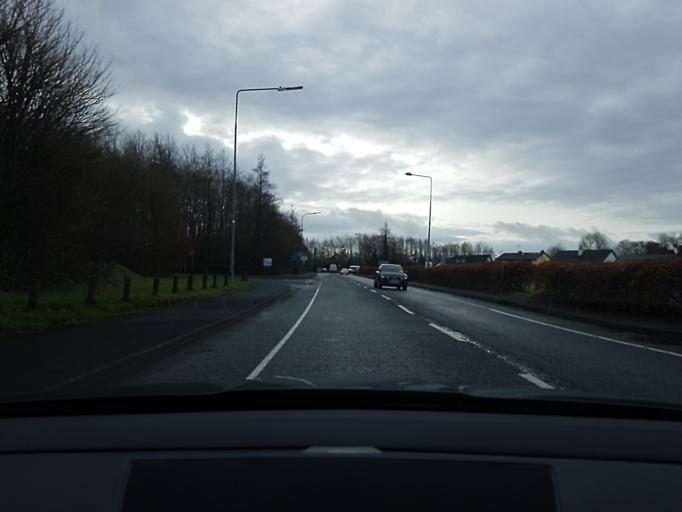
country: IE
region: Connaught
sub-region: Maigh Eo
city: Castlebar
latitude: 53.8505
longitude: -9.3089
